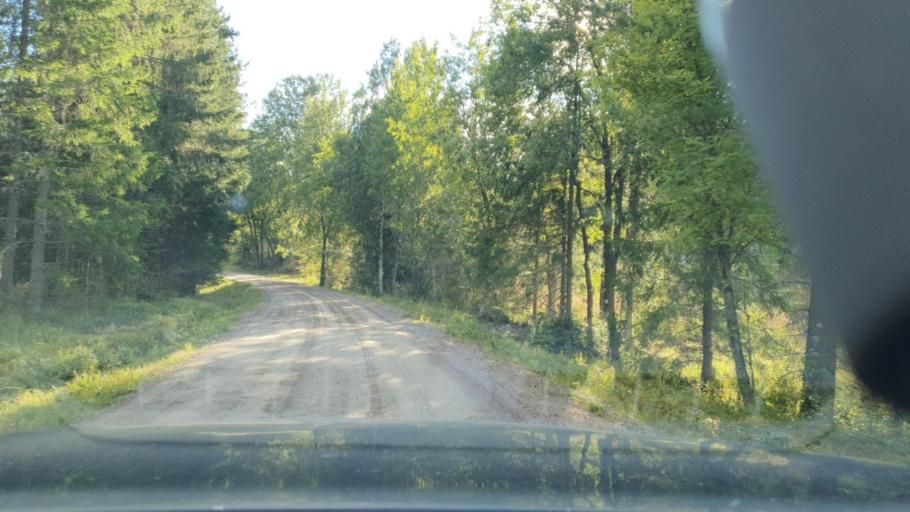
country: SE
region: Vaermland
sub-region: Karlstads Kommun
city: Molkom
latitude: 59.6512
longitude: 13.8703
